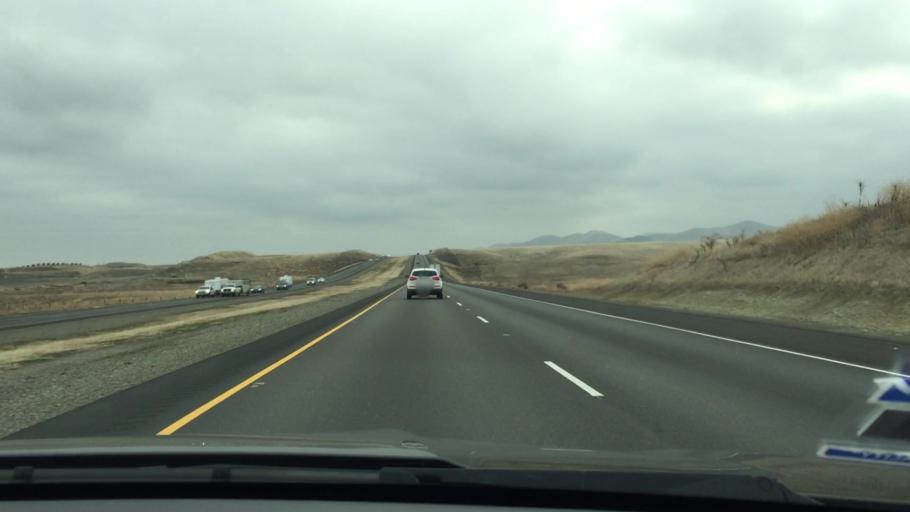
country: US
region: California
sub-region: Stanislaus County
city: Newman
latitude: 37.2736
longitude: -121.0961
